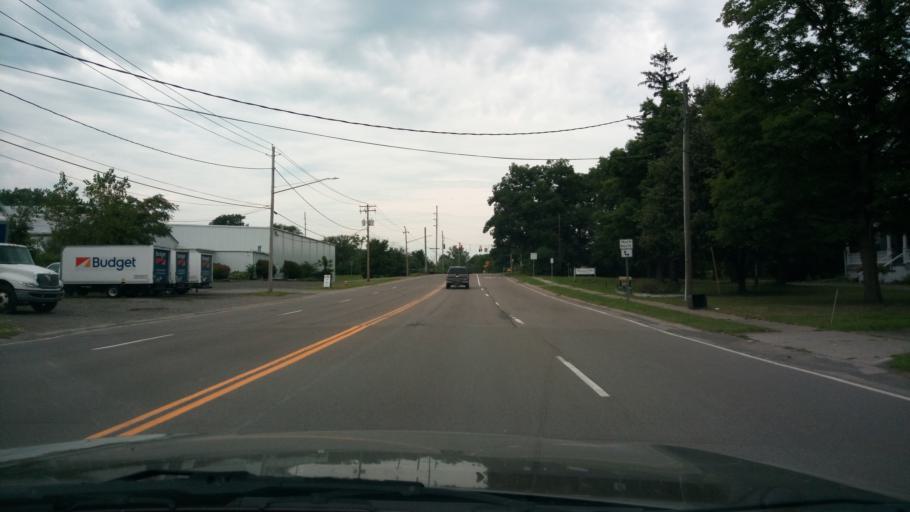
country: US
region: New York
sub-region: Chemung County
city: Elmira Heights
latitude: 42.1141
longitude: -76.8127
